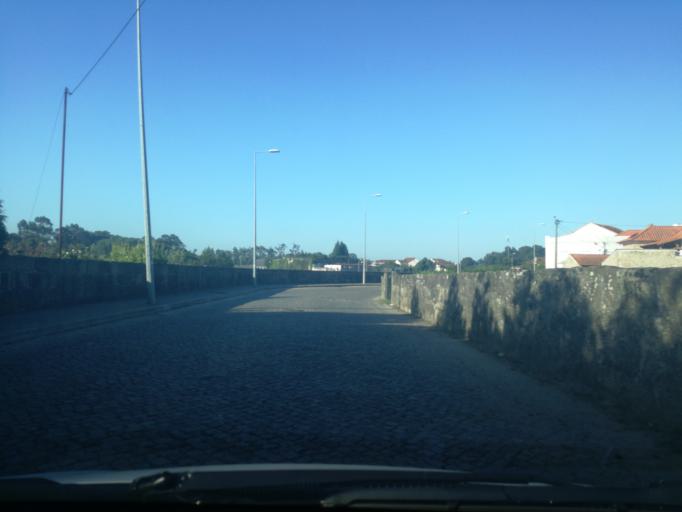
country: PT
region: Porto
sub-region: Maia
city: Milheiros
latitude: 41.2142
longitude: -8.5919
